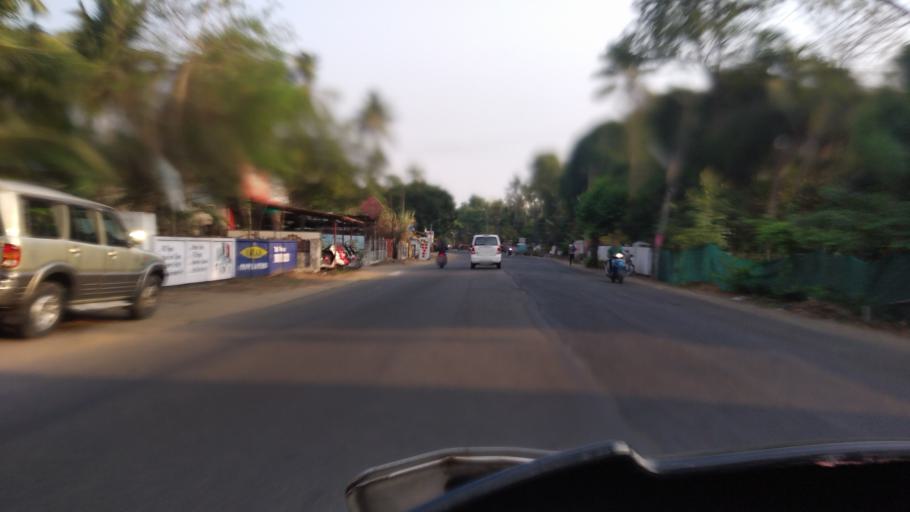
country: IN
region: Kerala
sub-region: Thrissur District
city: Thanniyam
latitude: 10.3888
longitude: 76.1192
